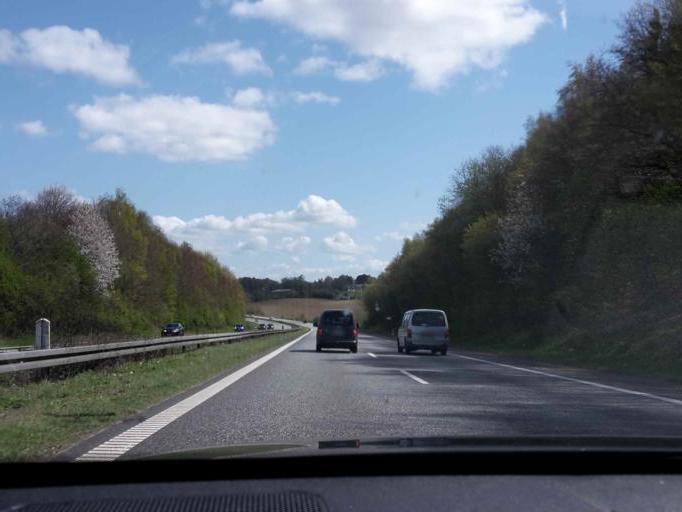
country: DK
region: South Denmark
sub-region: Fredericia Kommune
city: Taulov
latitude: 55.5439
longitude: 9.5858
